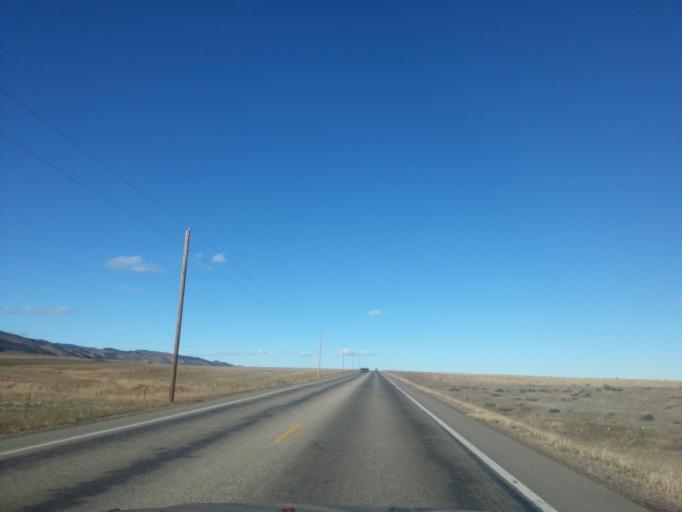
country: US
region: Colorado
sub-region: Larimer County
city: Loveland
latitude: 40.4598
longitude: -105.1156
